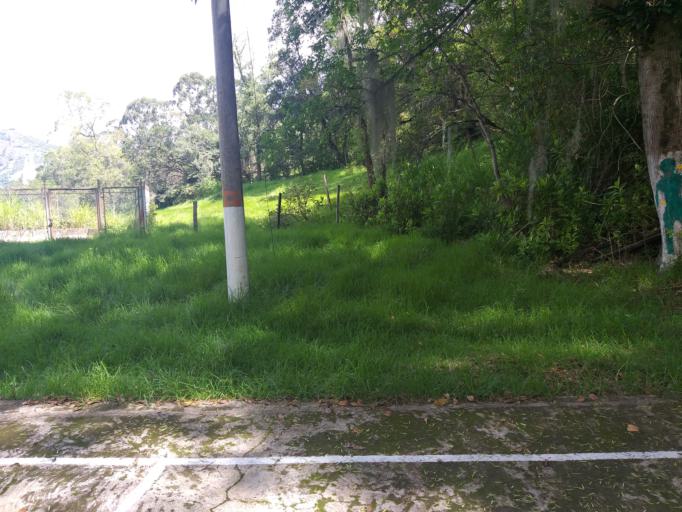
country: CO
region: Boyaca
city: Boavita
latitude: 6.3276
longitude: -72.5801
